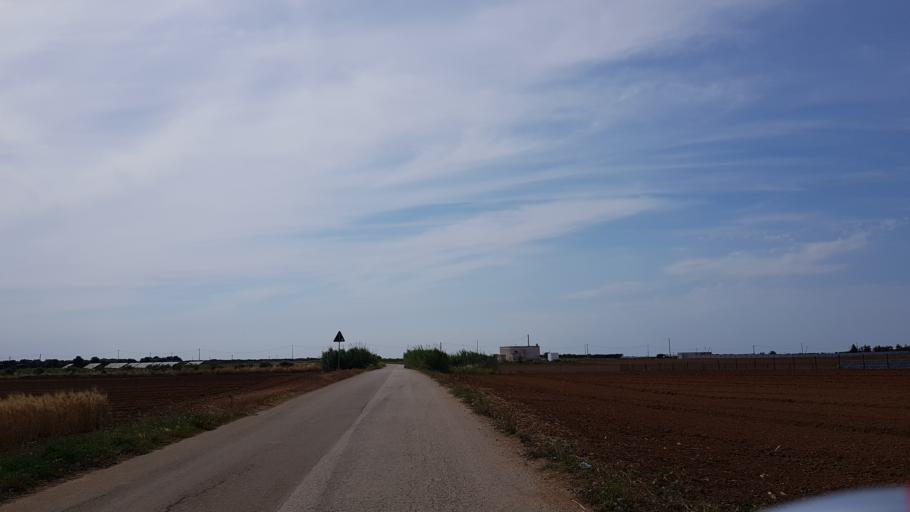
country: IT
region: Apulia
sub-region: Provincia di Brindisi
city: Mesagne
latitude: 40.6654
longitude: 17.8153
